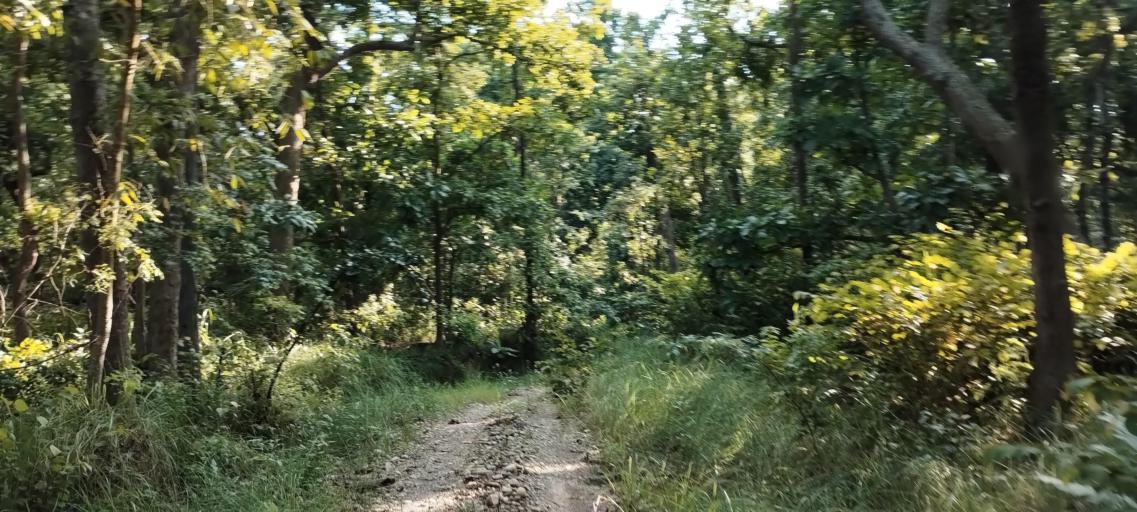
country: NP
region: Far Western
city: Tikapur
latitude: 28.5191
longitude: 81.2758
